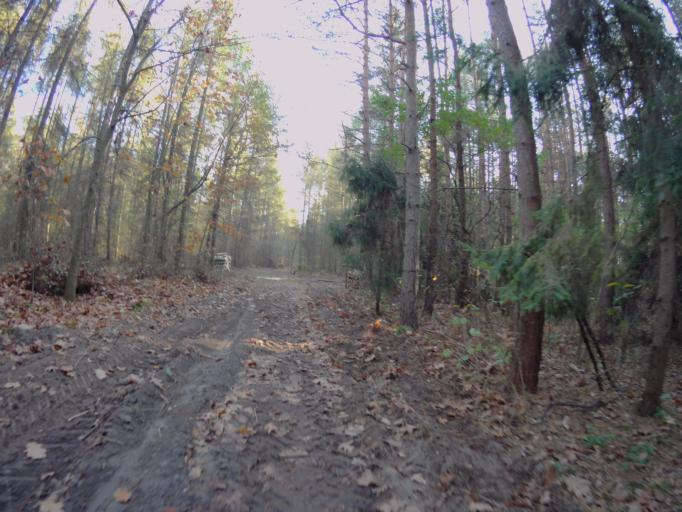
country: PL
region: Subcarpathian Voivodeship
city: Nowa Sarzyna
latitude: 50.3072
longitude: 22.3528
